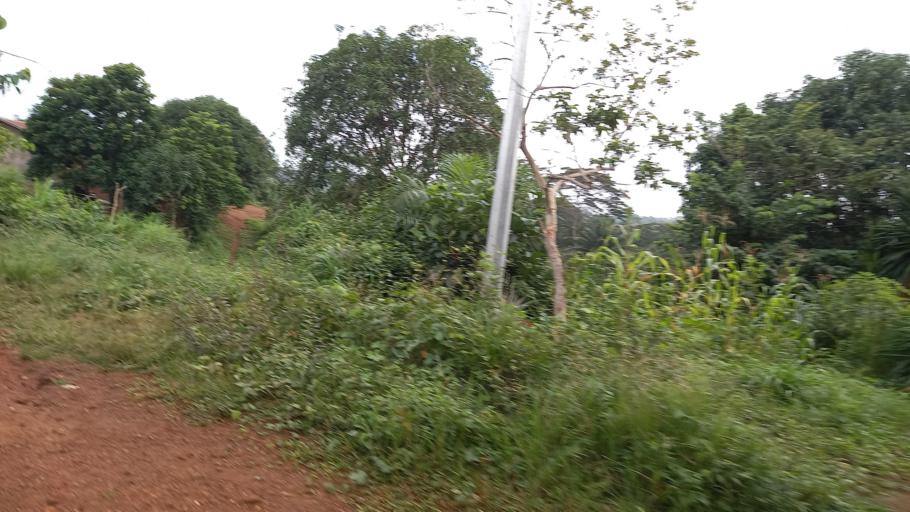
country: SL
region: Eastern Province
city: Kailahun
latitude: 8.2779
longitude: -10.5843
